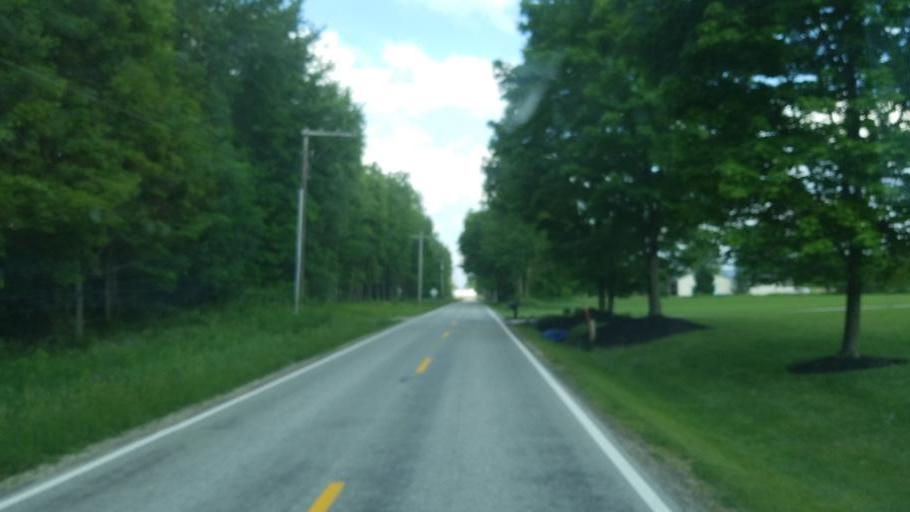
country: US
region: Ohio
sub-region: Delaware County
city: Sunbury
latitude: 40.2187
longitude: -82.8607
